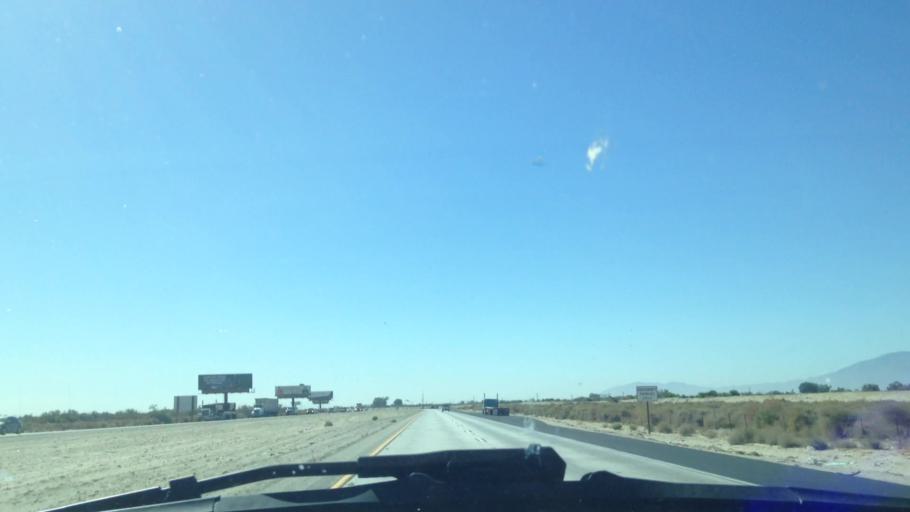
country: US
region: California
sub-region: Riverside County
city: Coachella
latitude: 33.6999
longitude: -116.1750
